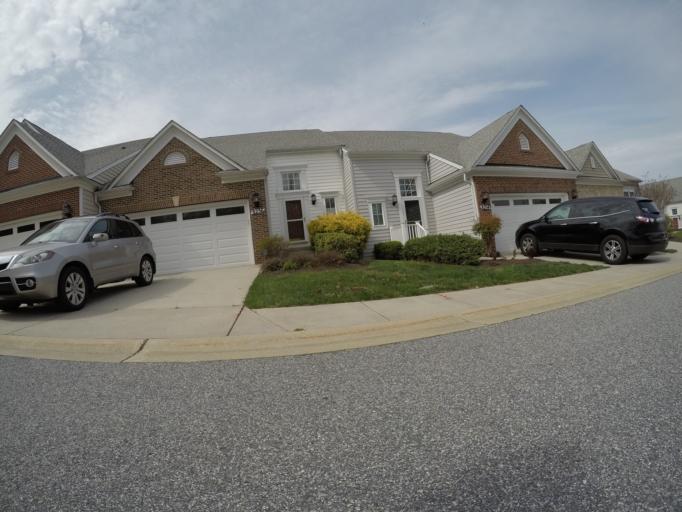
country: US
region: Maryland
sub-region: Howard County
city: Ellicott City
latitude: 39.2509
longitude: -76.7882
